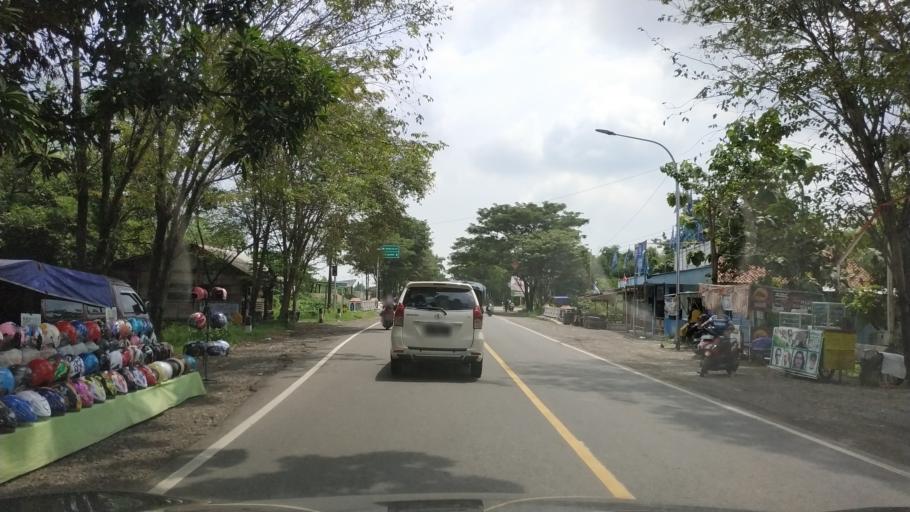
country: ID
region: Central Java
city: Slawi
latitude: -7.0091
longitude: 109.1410
